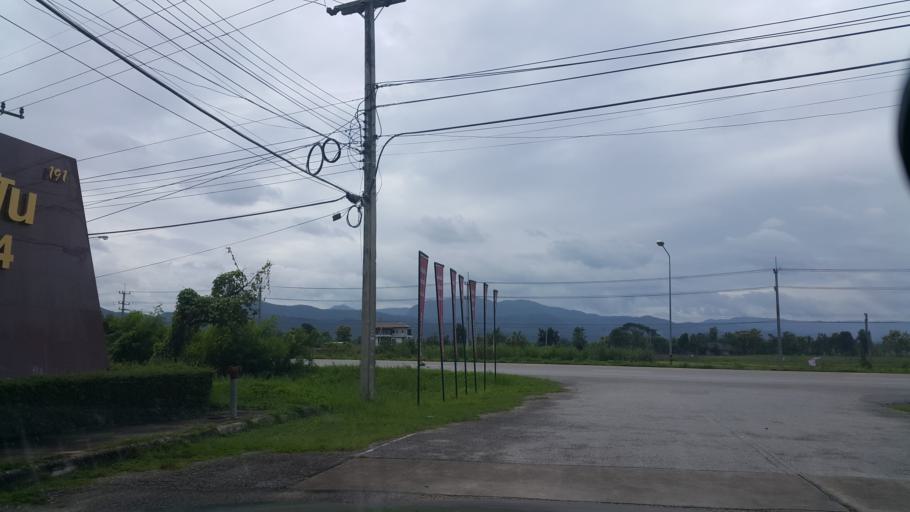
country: TH
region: Chiang Mai
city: San Kamphaeng
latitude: 18.7142
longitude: 99.1398
